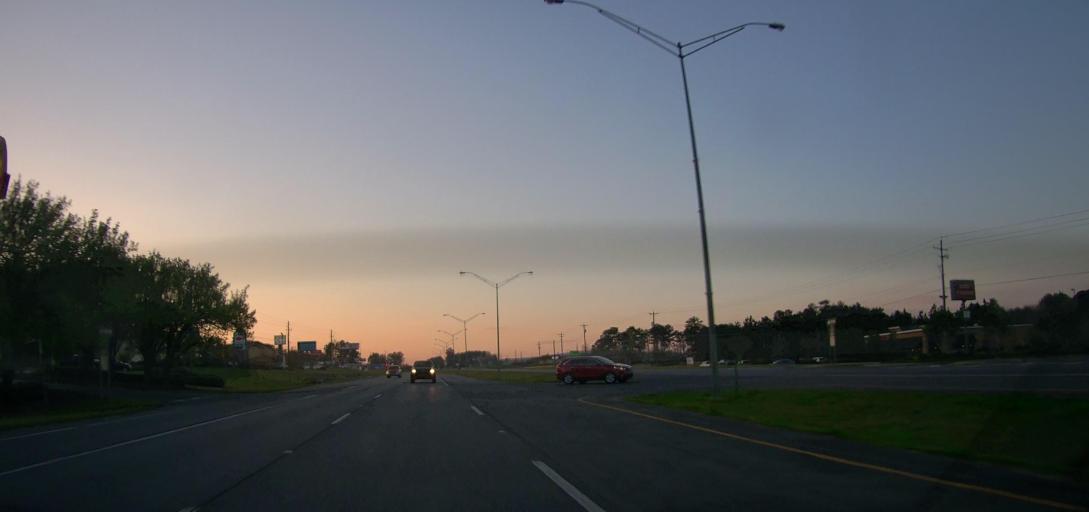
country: US
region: Alabama
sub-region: Tallapoosa County
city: Alexander City
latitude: 32.9227
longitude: -85.9598
